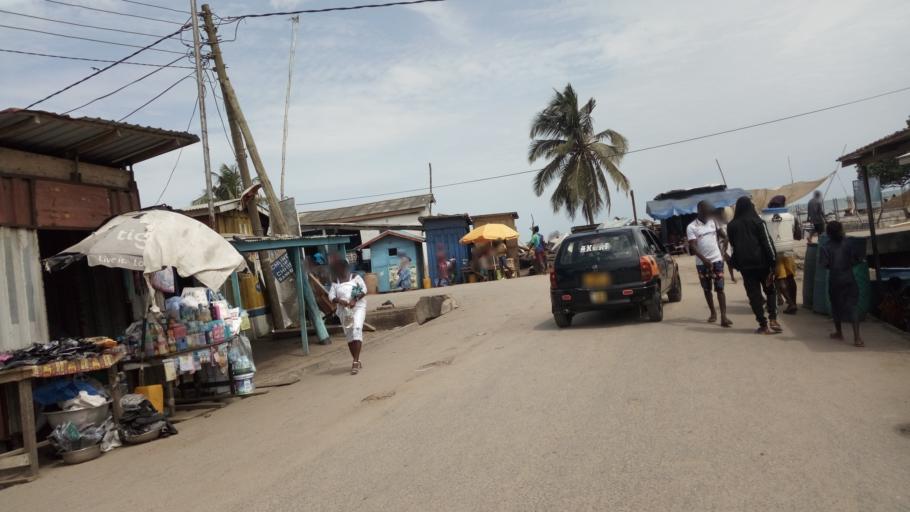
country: GH
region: Central
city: Winneba
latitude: 5.3434
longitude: -0.6174
